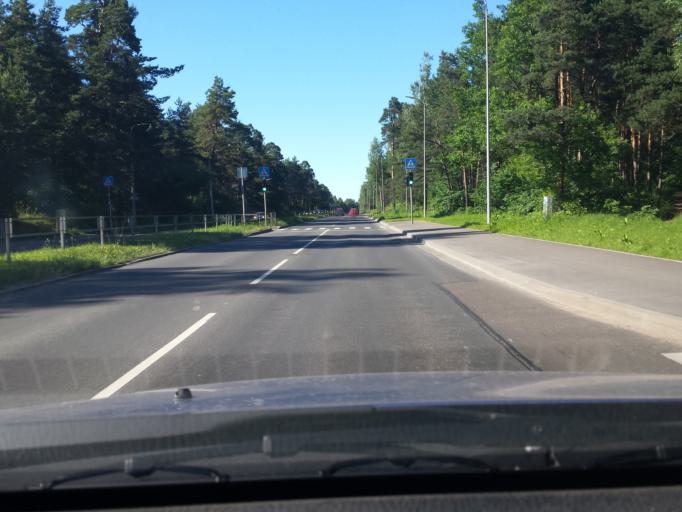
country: LV
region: Riga
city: Jaunciems
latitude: 57.0098
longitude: 24.1292
